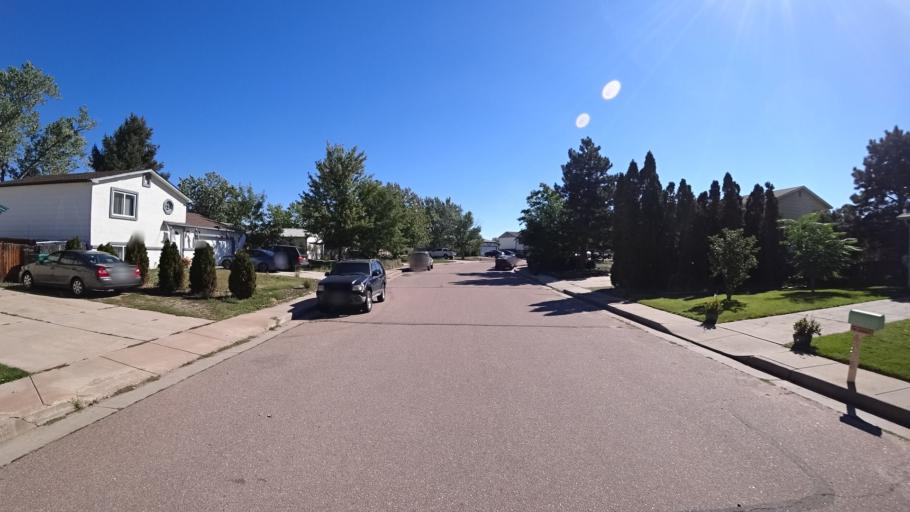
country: US
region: Colorado
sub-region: El Paso County
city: Cimarron Hills
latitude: 38.8181
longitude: -104.7350
